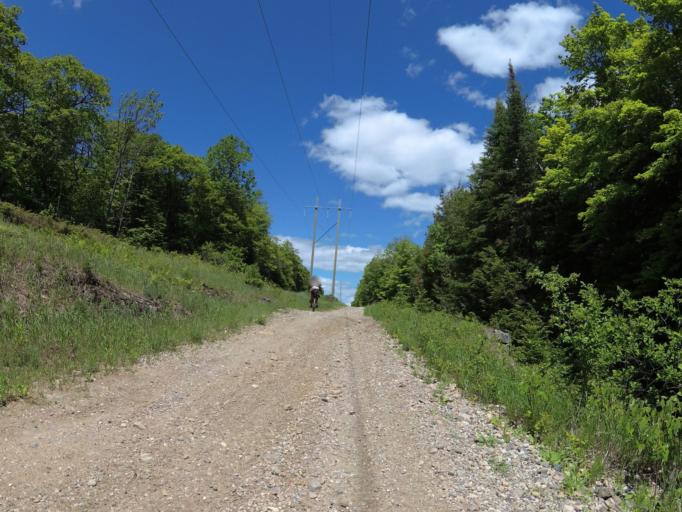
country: CA
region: Ontario
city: Renfrew
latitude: 45.0224
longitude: -76.8881
